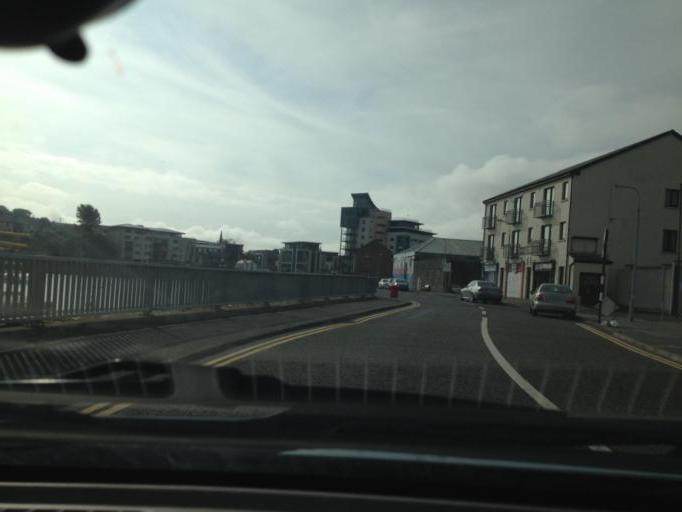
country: IE
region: Connaught
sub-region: Sligo
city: Sligo
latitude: 54.2748
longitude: -8.4784
